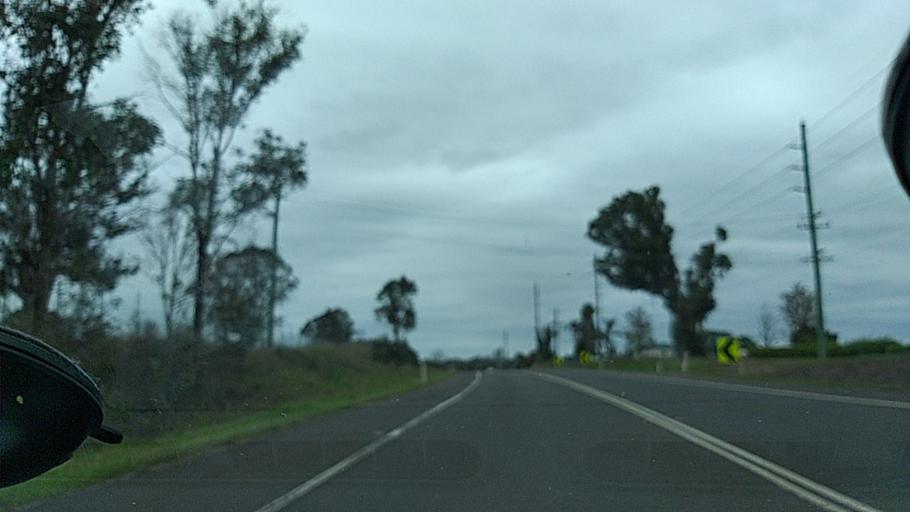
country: AU
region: New South Wales
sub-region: Penrith Municipality
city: Glenmore Park
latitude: -33.8158
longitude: 150.6889
